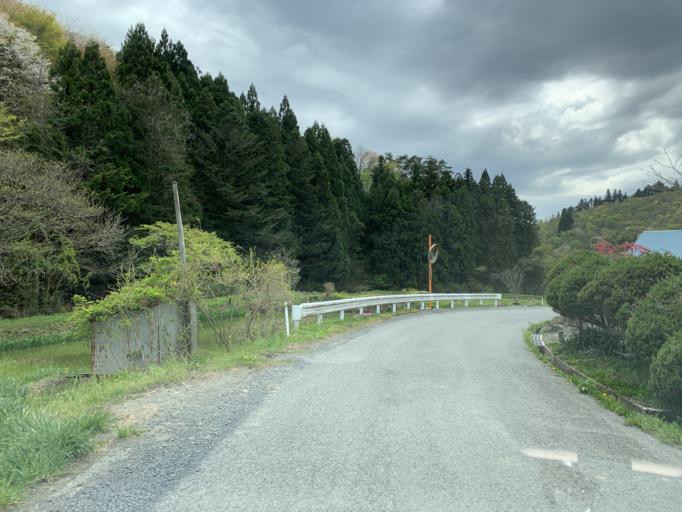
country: JP
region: Iwate
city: Ichinoseki
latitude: 38.7856
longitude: 141.4249
